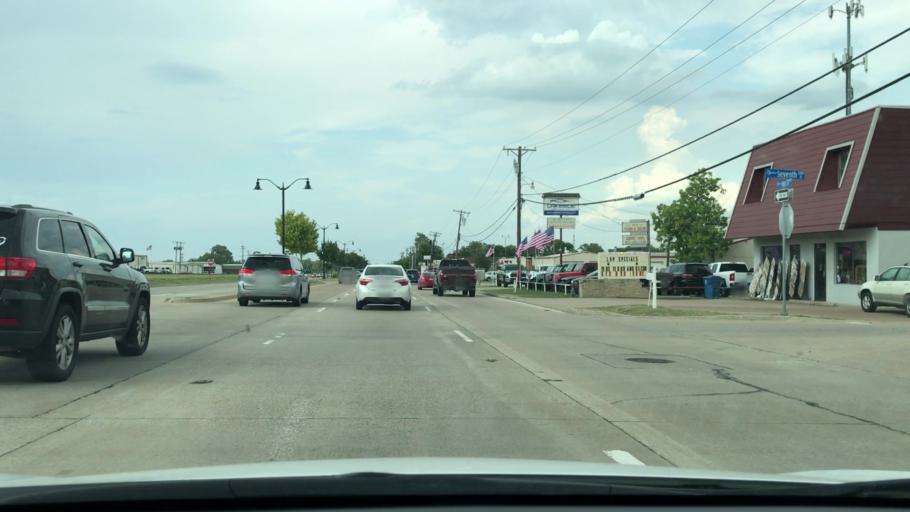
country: US
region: Texas
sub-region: Dallas County
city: Sachse
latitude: 32.9779
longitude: -96.5928
